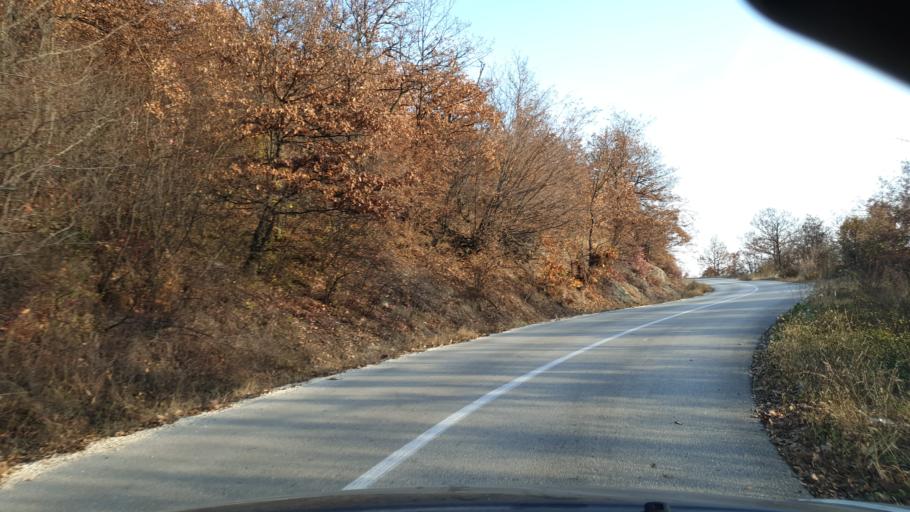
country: RS
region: Central Serbia
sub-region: Borski Okrug
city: Bor
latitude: 44.0479
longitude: 22.0773
